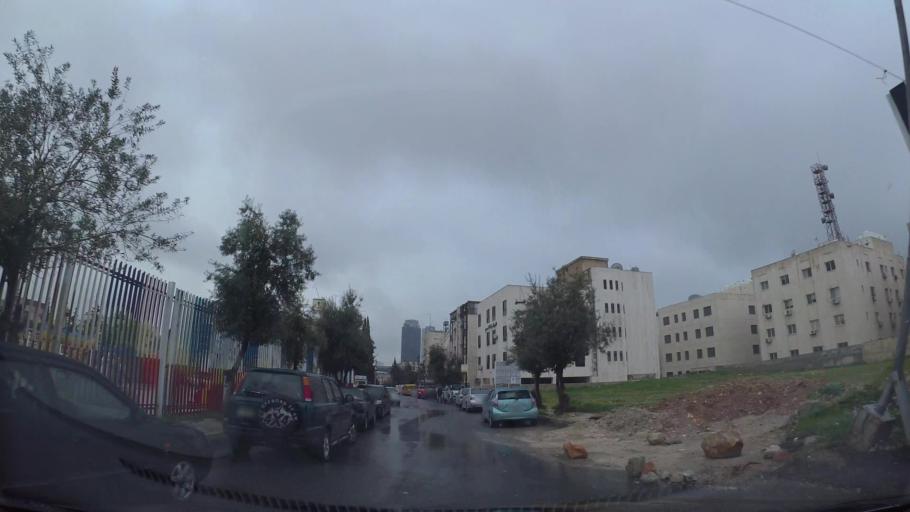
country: JO
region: Amman
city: Amman
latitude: 31.9711
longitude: 35.9117
